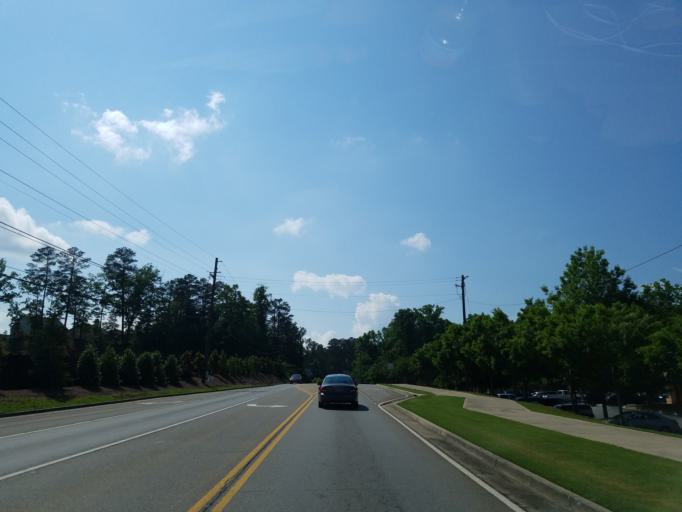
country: US
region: Georgia
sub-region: Cherokee County
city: Holly Springs
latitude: 34.1361
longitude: -84.5002
